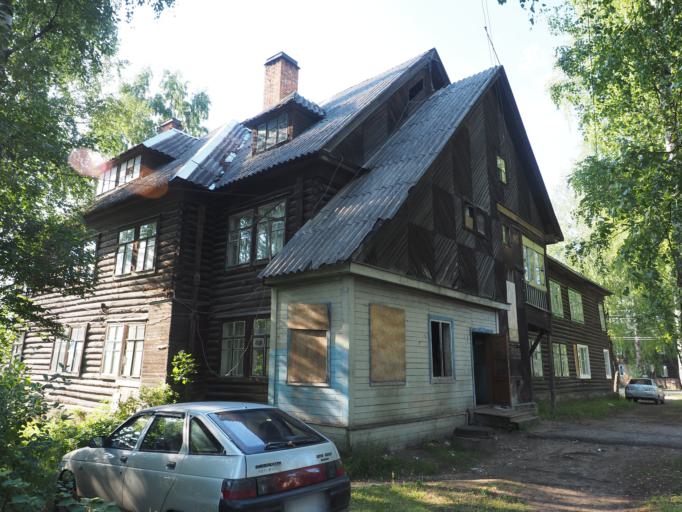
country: RU
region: Vologda
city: Chagoda
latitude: 59.1664
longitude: 35.3281
